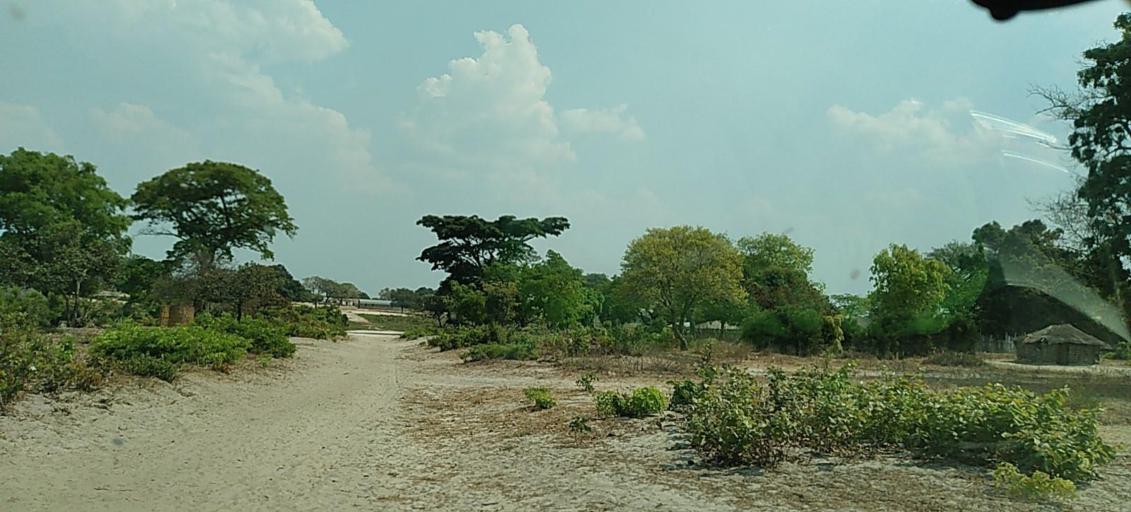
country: ZM
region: North-Western
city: Kabompo
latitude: -13.4463
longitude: 23.6676
